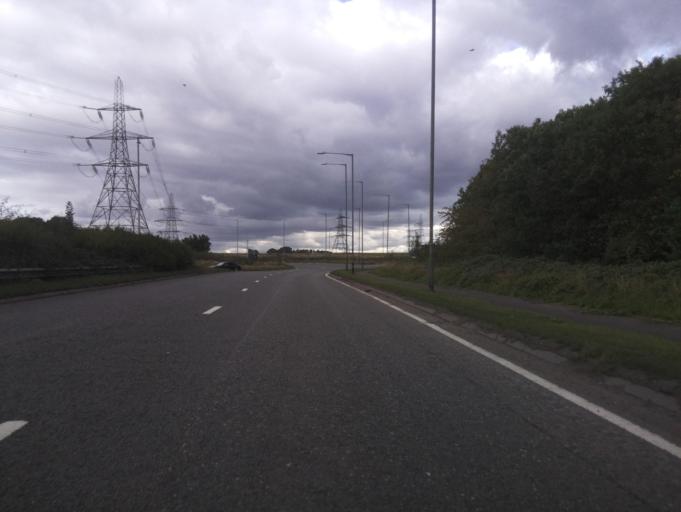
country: GB
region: England
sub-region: Warwickshire
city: Curdworth
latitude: 52.5287
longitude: -1.7227
